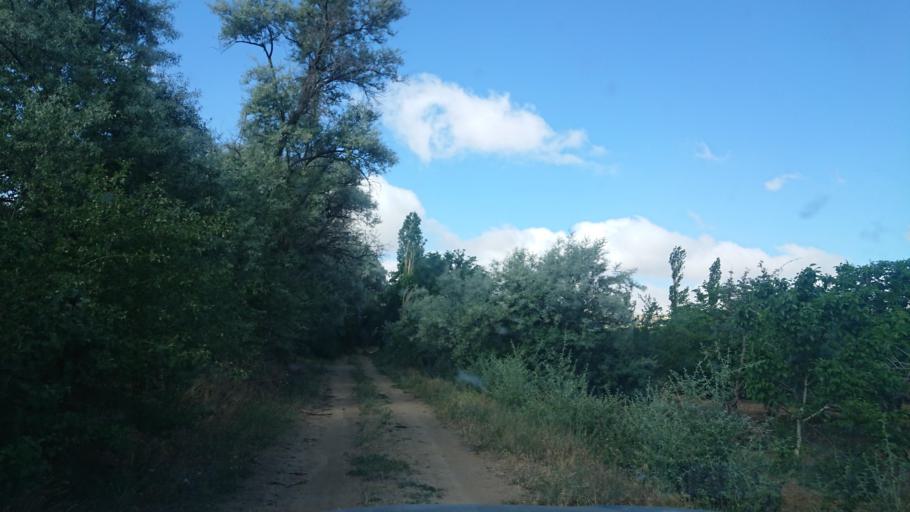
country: TR
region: Aksaray
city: Agacoren
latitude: 38.8485
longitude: 33.9314
